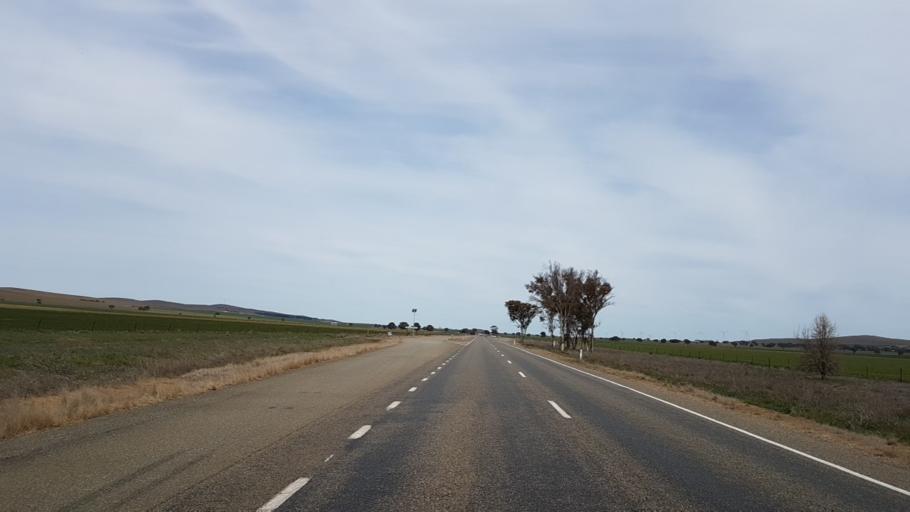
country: AU
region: South Australia
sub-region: Northern Areas
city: Jamestown
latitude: -33.0550
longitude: 138.6177
